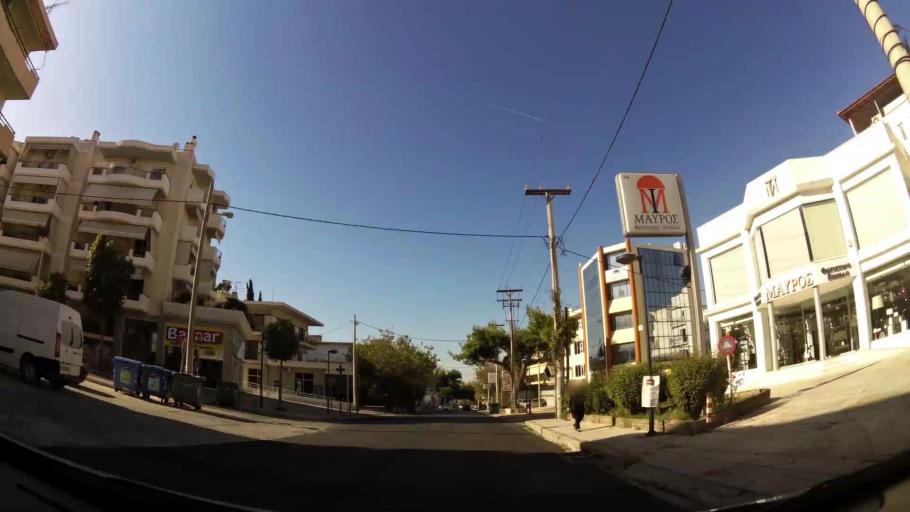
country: GR
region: Attica
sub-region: Nomarchia Athinas
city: Metamorfosi
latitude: 38.0678
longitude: 23.7698
